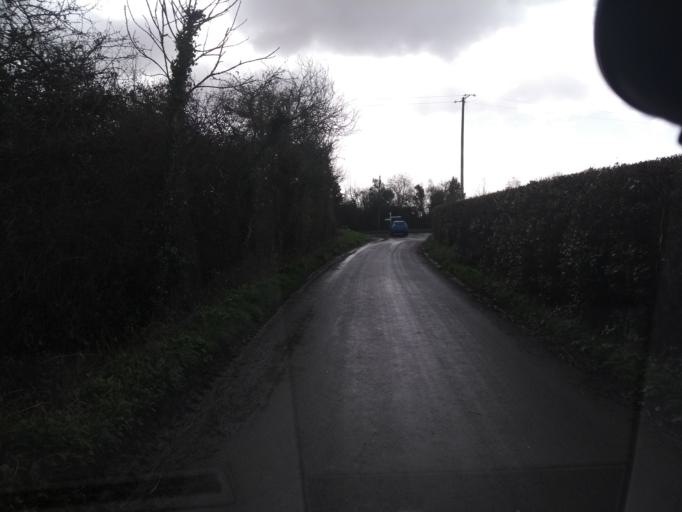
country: GB
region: England
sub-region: Somerset
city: South Petherton
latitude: 50.9693
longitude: -2.8093
